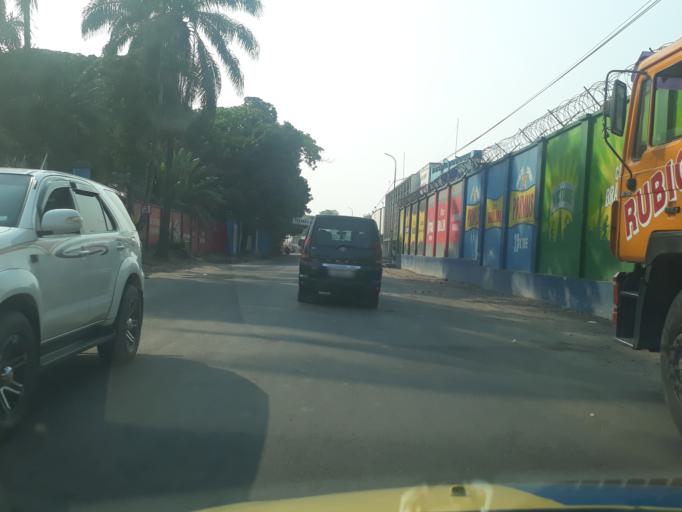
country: CD
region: Kinshasa
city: Kinshasa
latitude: -4.3085
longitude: 15.3267
